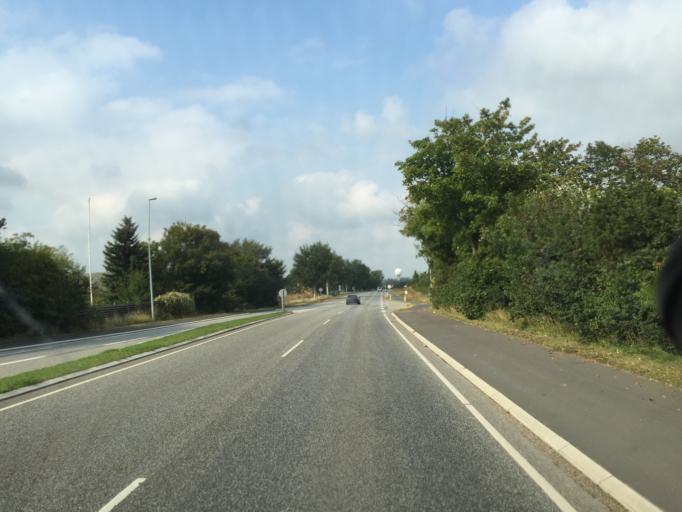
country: DK
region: Zealand
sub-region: Solrod Kommune
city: Havdrup
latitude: 55.5726
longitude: 12.1135
